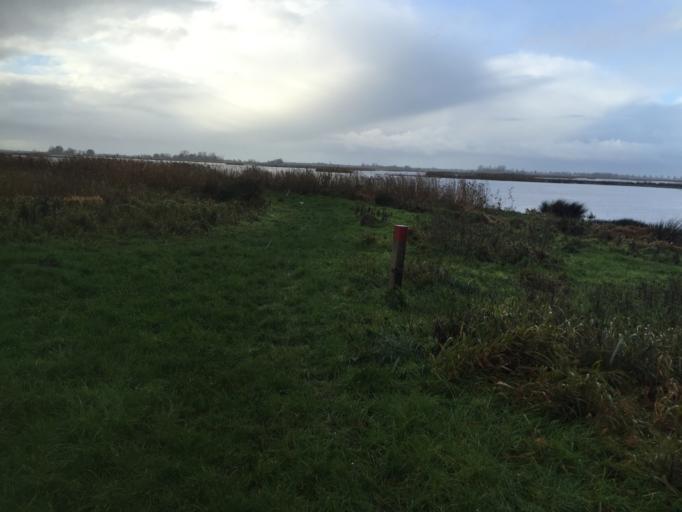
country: NL
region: Utrecht
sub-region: Gemeente De Ronde Venen
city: Mijdrecht
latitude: 52.1821
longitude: 4.8306
